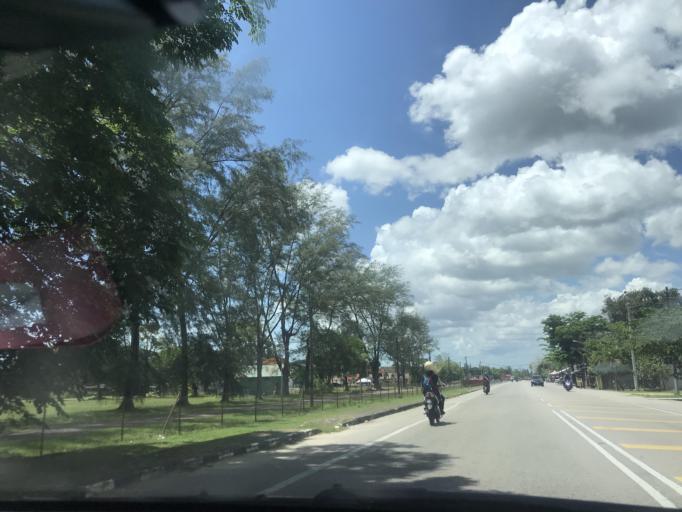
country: MY
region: Kelantan
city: Tumpat
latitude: 6.1910
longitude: 102.1543
